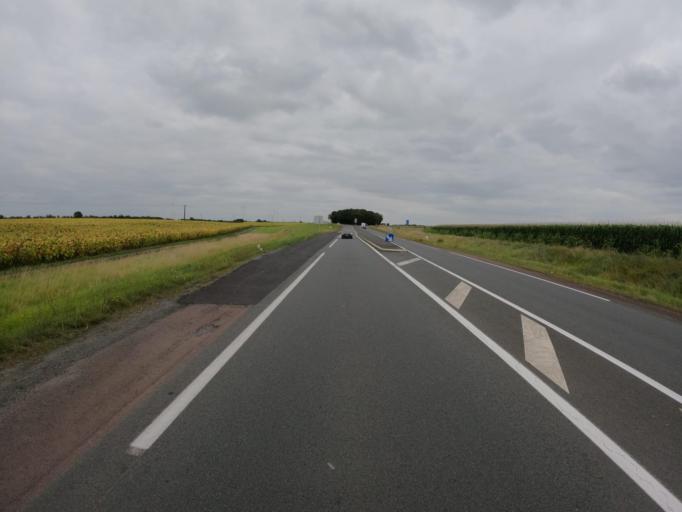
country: FR
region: Pays de la Loire
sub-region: Departement de la Vendee
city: Benet
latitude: 46.3920
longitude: -0.6399
